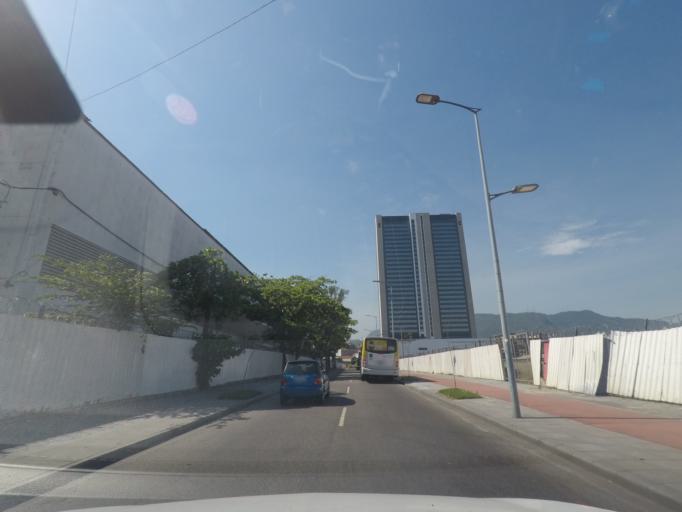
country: BR
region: Rio de Janeiro
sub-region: Rio De Janeiro
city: Rio de Janeiro
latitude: -22.9007
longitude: -43.2065
